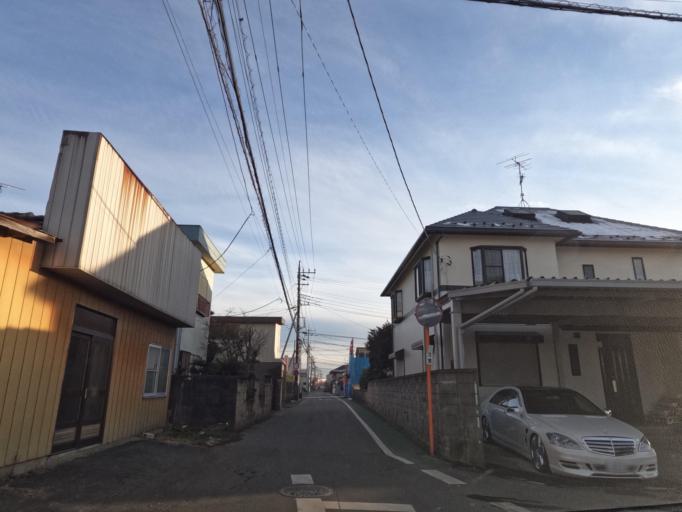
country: JP
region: Ibaraki
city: Mitsukaido
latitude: 35.9910
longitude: 140.0575
